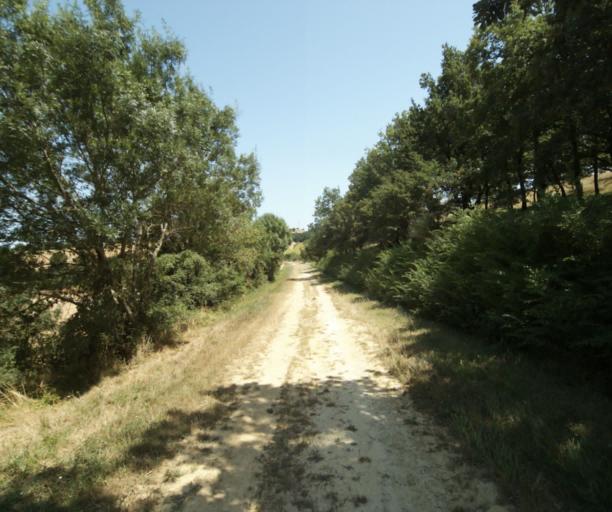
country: FR
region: Midi-Pyrenees
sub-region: Departement de la Haute-Garonne
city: Saint-Felix-Lauragais
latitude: 43.4413
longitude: 1.8729
